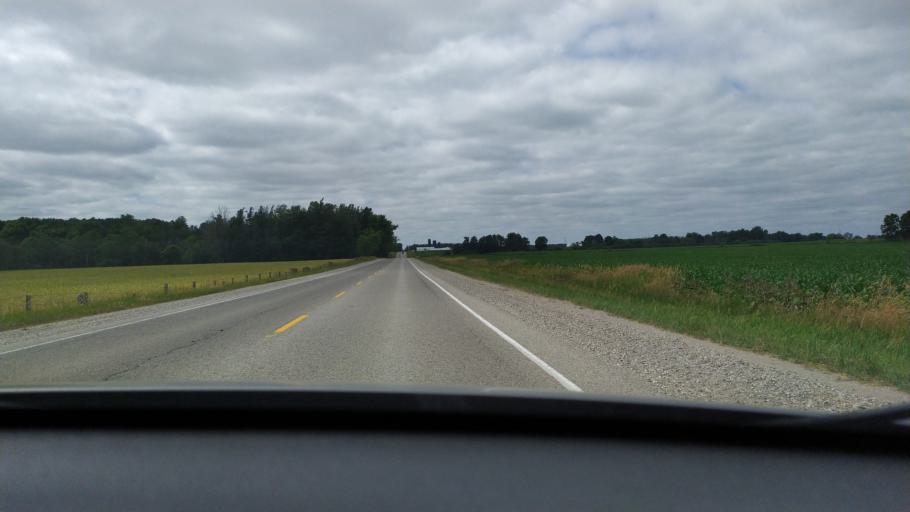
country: CA
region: Ontario
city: Stratford
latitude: 43.3214
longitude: -80.9546
